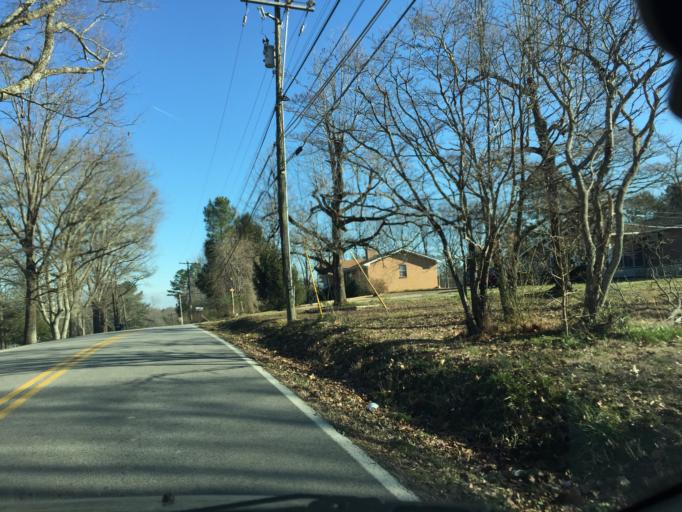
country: US
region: Tennessee
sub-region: Hamilton County
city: Collegedale
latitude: 35.0421
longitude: -85.0999
